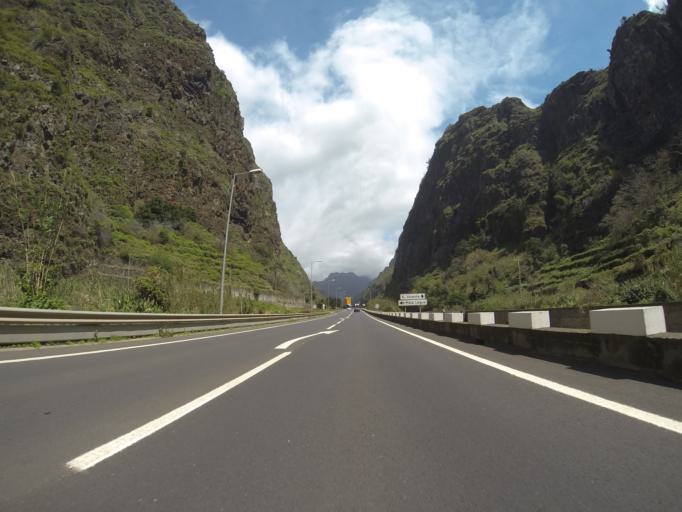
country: PT
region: Madeira
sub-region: Ribeira Brava
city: Campanario
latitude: 32.7024
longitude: -17.0402
